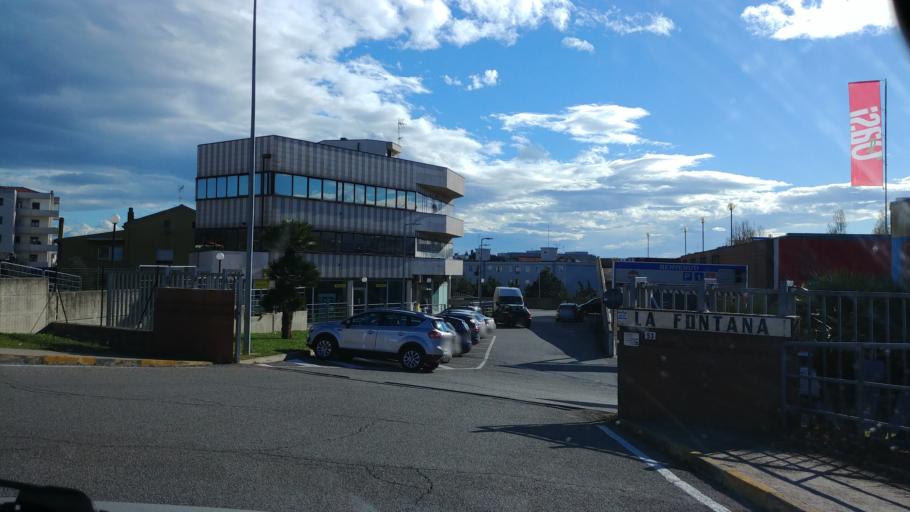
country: IT
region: Molise
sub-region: Provincia di Campobasso
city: Termoli
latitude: 41.9954
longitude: 14.9832
